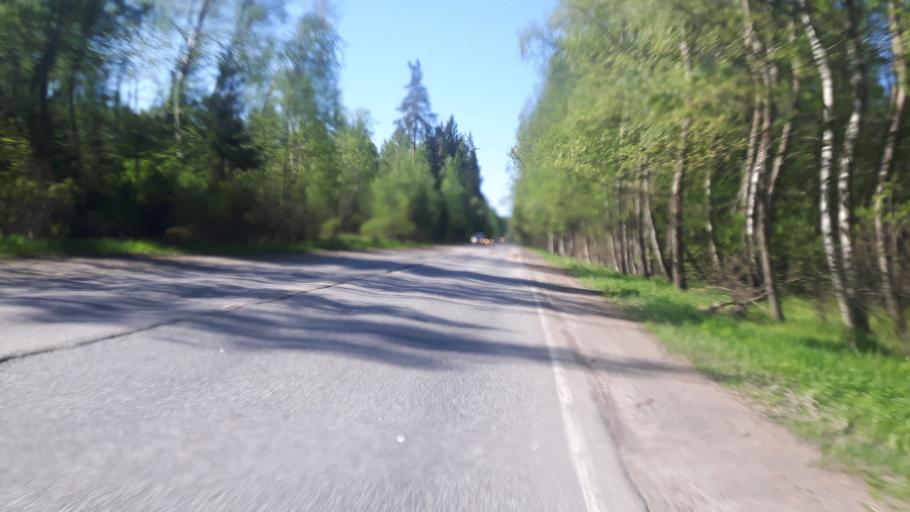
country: RU
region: Leningrad
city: Vyborg
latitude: 60.6428
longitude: 28.7425
